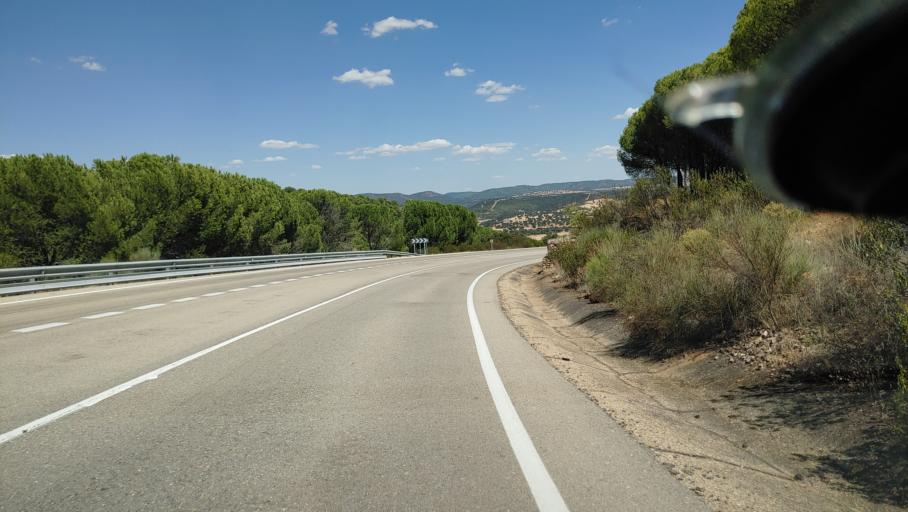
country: ES
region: Castille-La Mancha
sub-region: Provincia de Ciudad Real
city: Saceruela
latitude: 39.0070
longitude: -4.5114
